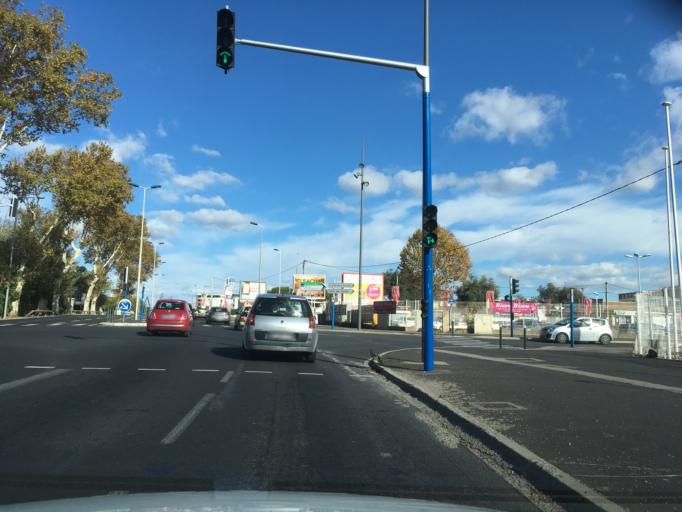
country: FR
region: Languedoc-Roussillon
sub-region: Departement de l'Herault
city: Saint-Jean-de-Vedas
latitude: 43.5877
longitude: 3.8541
